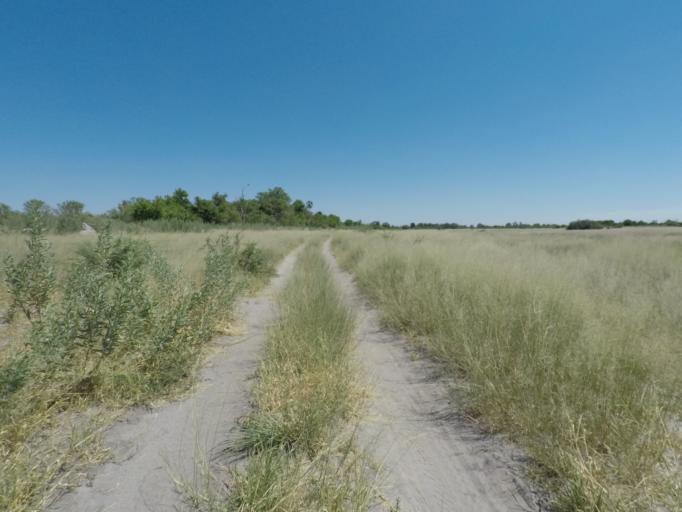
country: BW
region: North West
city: Maun
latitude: -19.4760
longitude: 23.5525
